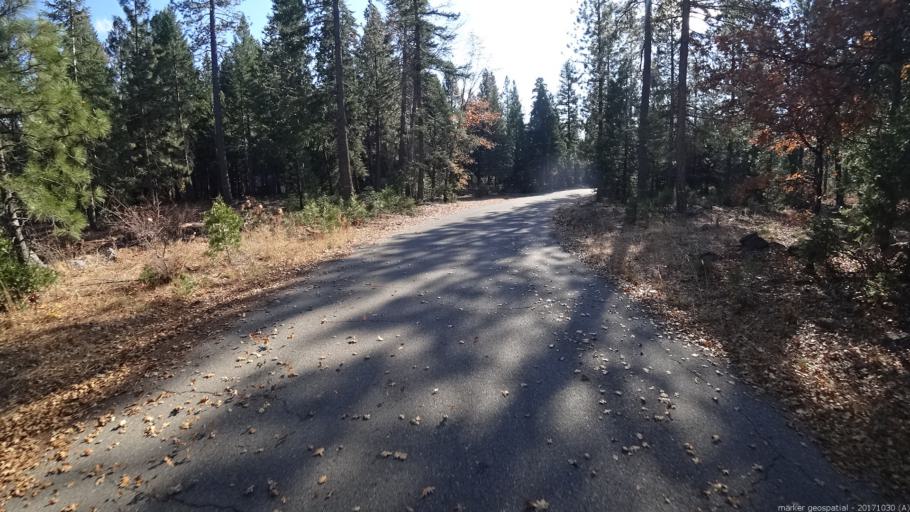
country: US
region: California
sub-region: Shasta County
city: Shingletown
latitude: 40.5124
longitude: -121.7317
